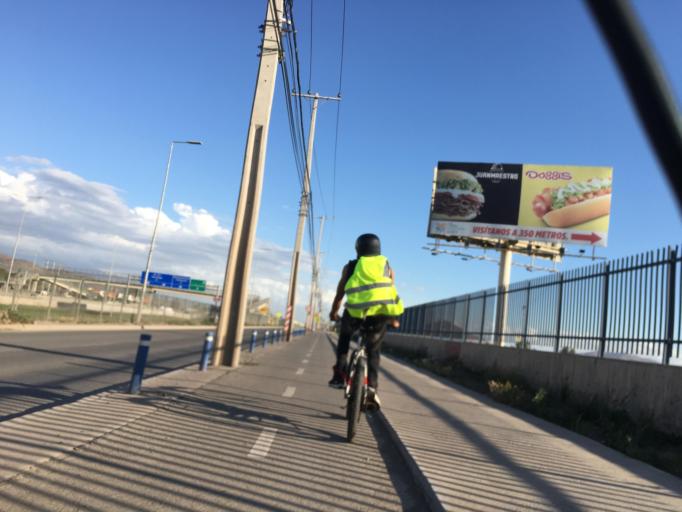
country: CL
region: Santiago Metropolitan
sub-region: Provincia de Chacabuco
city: Chicureo Abajo
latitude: -33.3078
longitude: -70.7270
